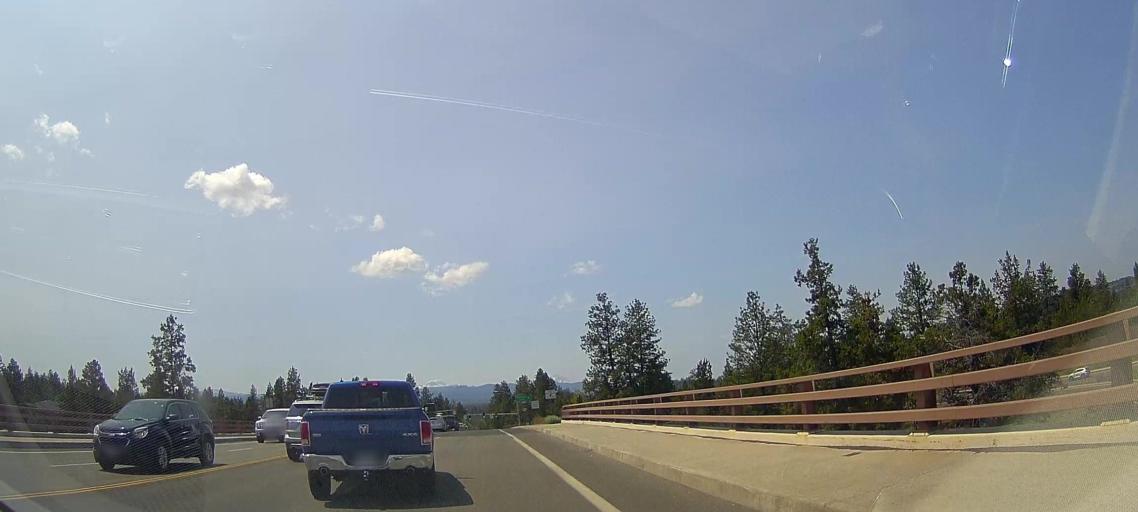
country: US
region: Oregon
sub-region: Deschutes County
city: Bend
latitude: 44.0387
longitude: -121.3080
